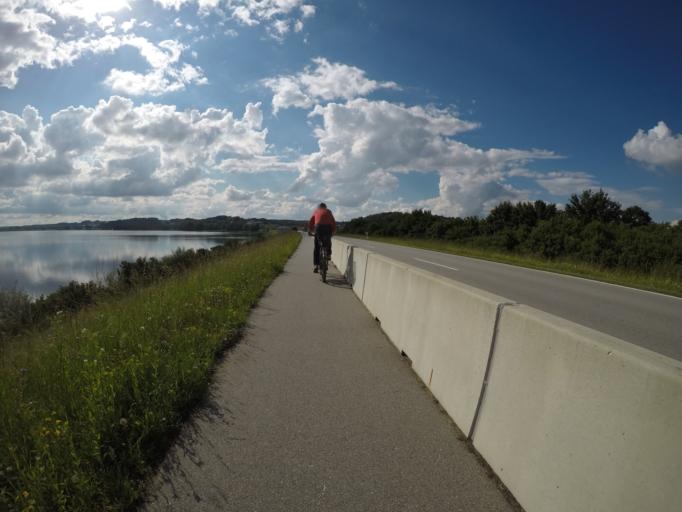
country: DE
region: Bavaria
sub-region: Lower Bavaria
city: Marklkofen
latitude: 48.5683
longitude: 12.5939
